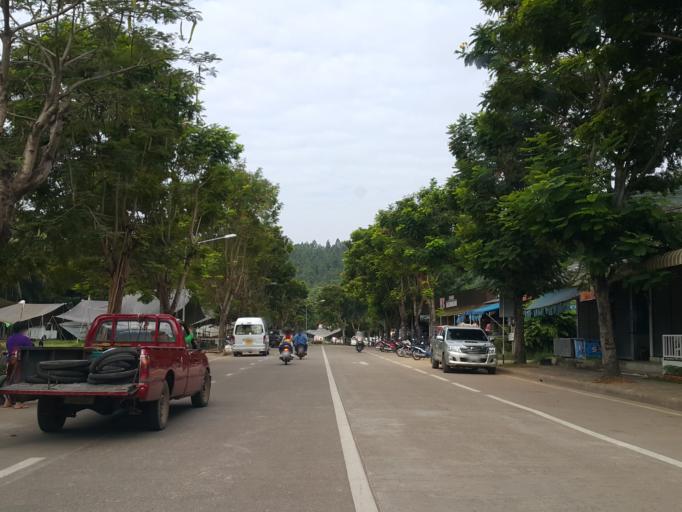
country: TH
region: Mae Hong Son
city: Mae Hong Son
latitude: 19.2926
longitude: 97.9644
